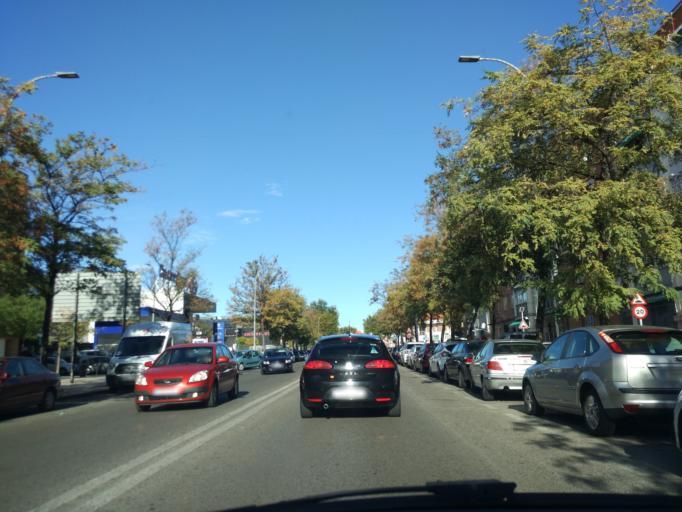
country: ES
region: Madrid
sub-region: Provincia de Madrid
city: Torrejon de Ardoz
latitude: 40.4496
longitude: -3.4698
